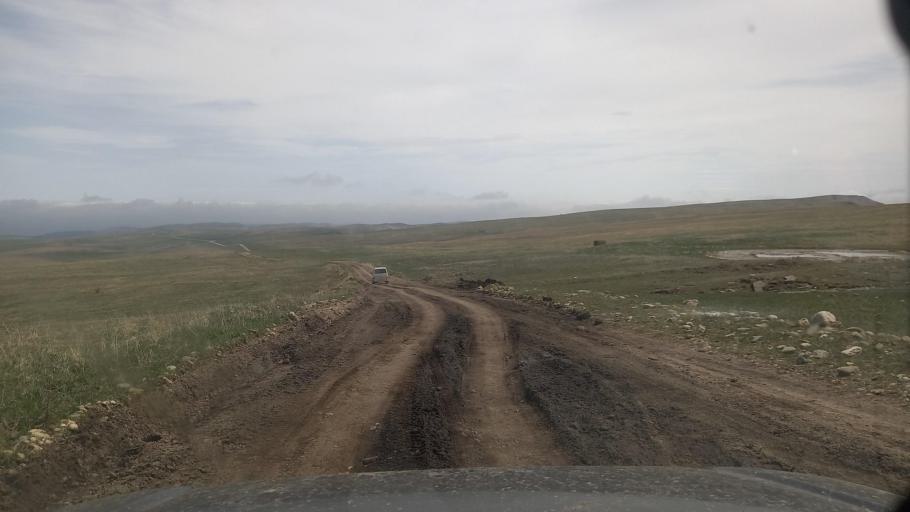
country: RU
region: Stavropol'skiy
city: Kislovodsk
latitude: 43.7579
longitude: 42.7707
